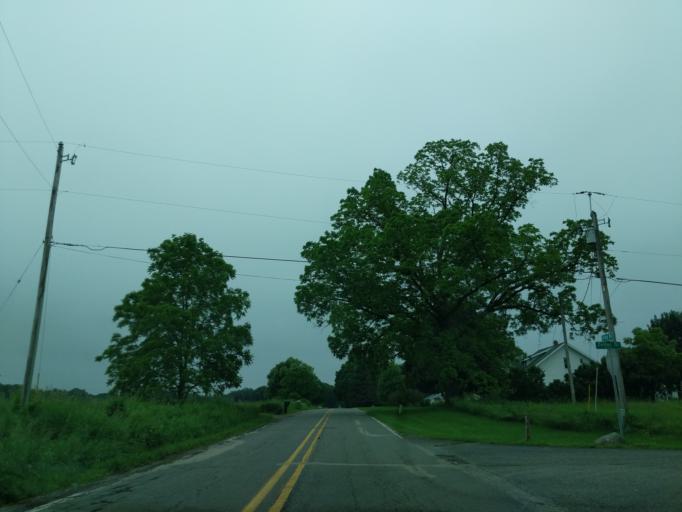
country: US
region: Michigan
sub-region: Jackson County
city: Spring Arbor
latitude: 42.2183
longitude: -84.5655
